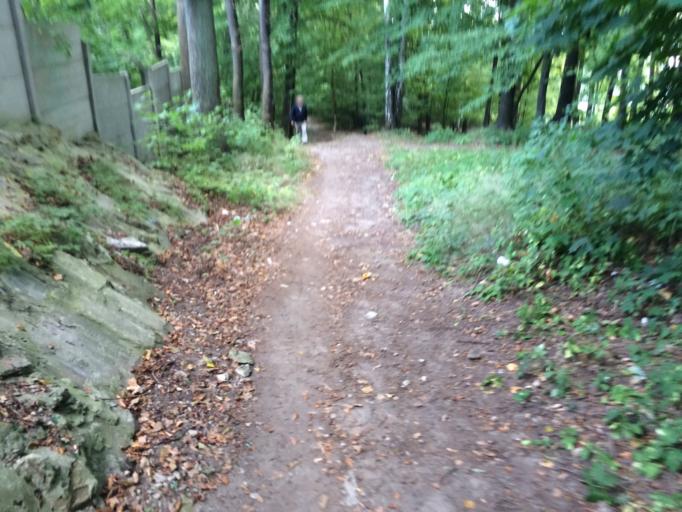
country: PL
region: Swietokrzyskie
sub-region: Powiat starachowicki
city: Starachowice
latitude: 51.0518
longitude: 21.0691
